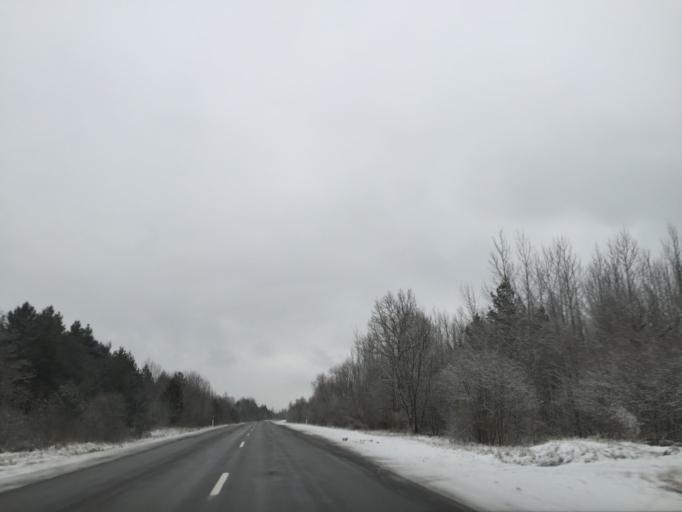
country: EE
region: Laeaene
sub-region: Lihula vald
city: Lihula
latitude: 58.6252
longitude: 23.8908
